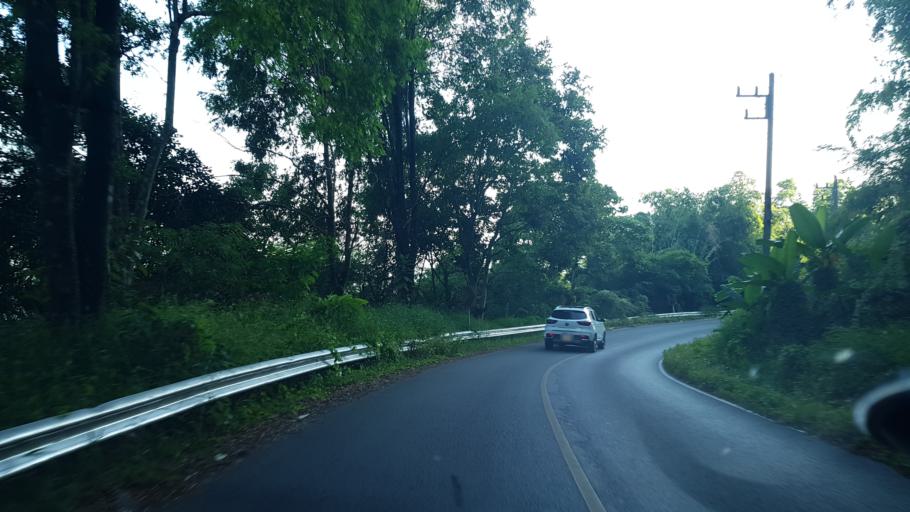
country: TH
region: Chiang Rai
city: Mae Fa Luang
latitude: 20.3188
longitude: 99.8184
